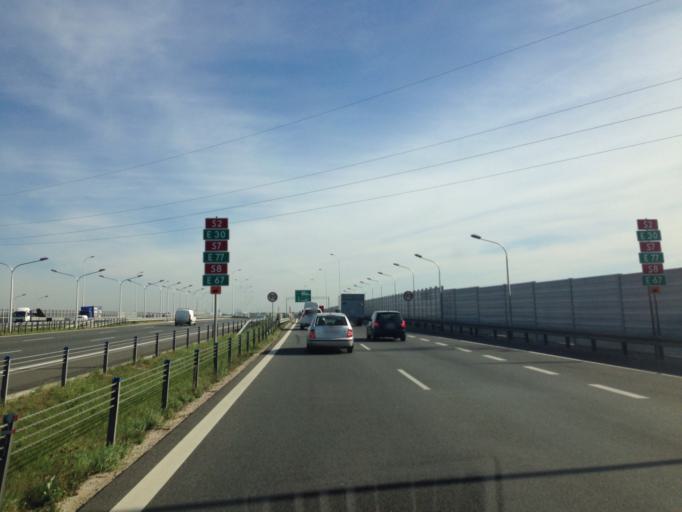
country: PL
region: Masovian Voivodeship
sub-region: Powiat pruszkowski
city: Michalowice
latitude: 52.1783
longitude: 20.8892
